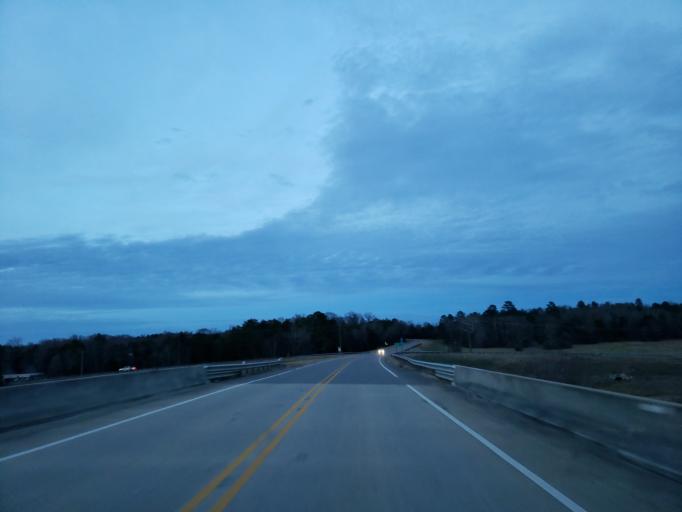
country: US
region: Alabama
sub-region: Greene County
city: Eutaw
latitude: 32.8586
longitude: -88.0993
